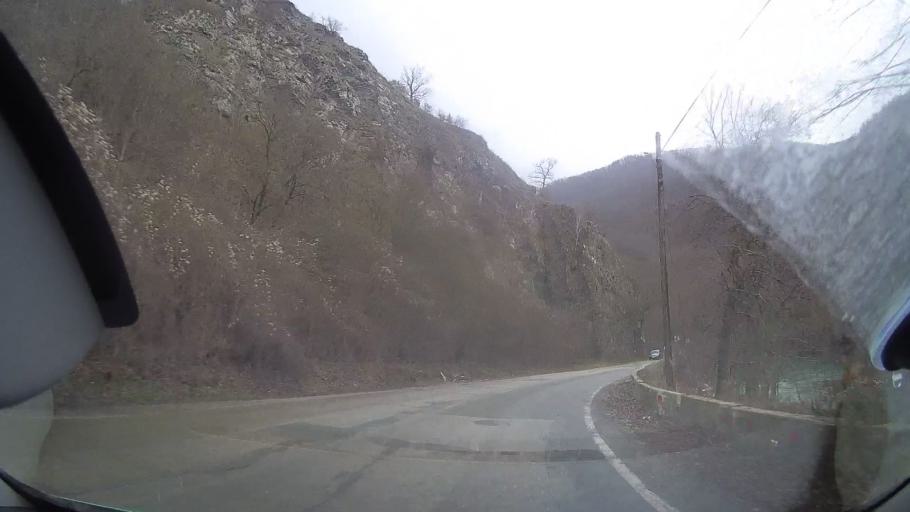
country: RO
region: Cluj
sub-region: Comuna Moldovenesti
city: Moldovenesti
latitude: 46.5044
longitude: 23.6233
